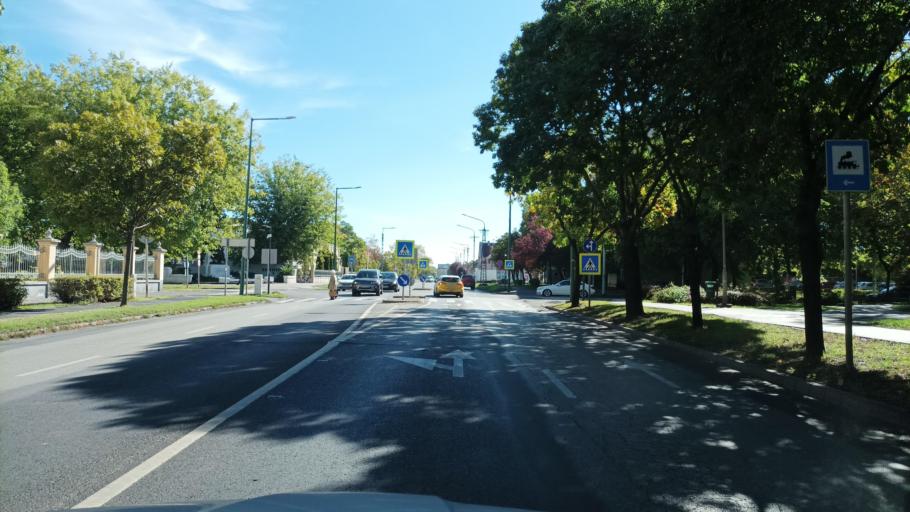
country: HU
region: Pest
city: Cegled
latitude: 47.1762
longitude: 19.8010
